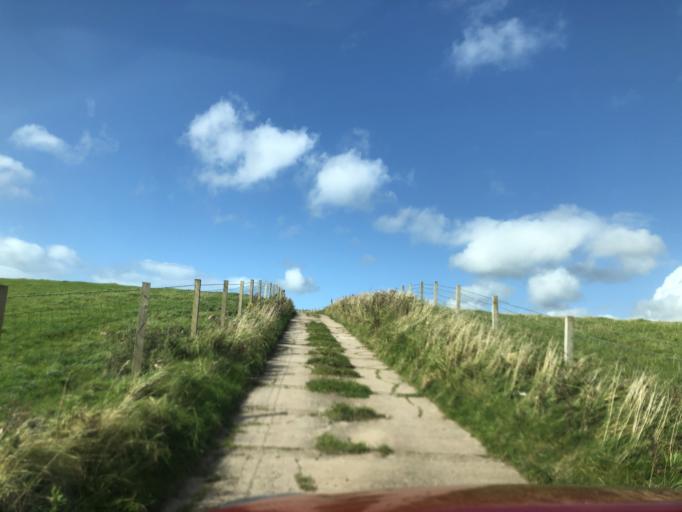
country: GB
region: Scotland
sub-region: Argyll and Bute
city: Campbeltown
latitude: 55.3112
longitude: -5.6065
